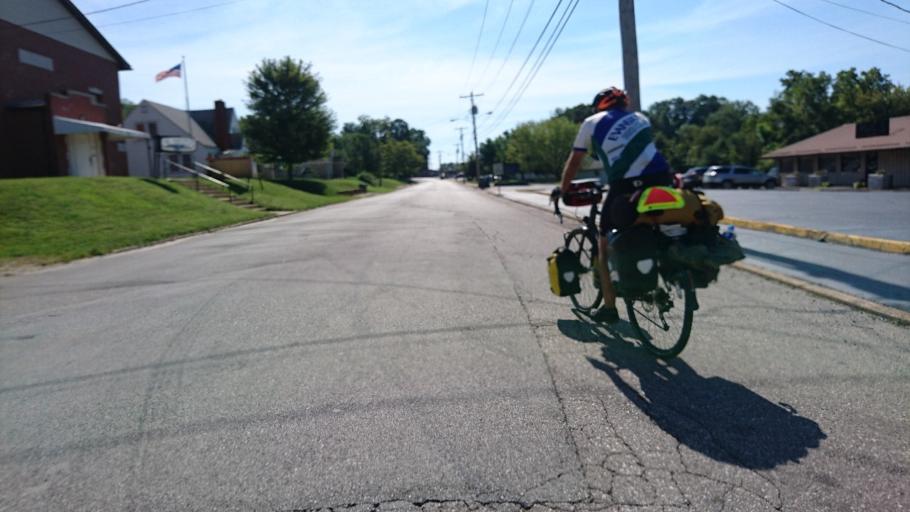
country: US
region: Missouri
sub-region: Franklin County
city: Saint Clair
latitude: 38.3506
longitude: -90.9826
